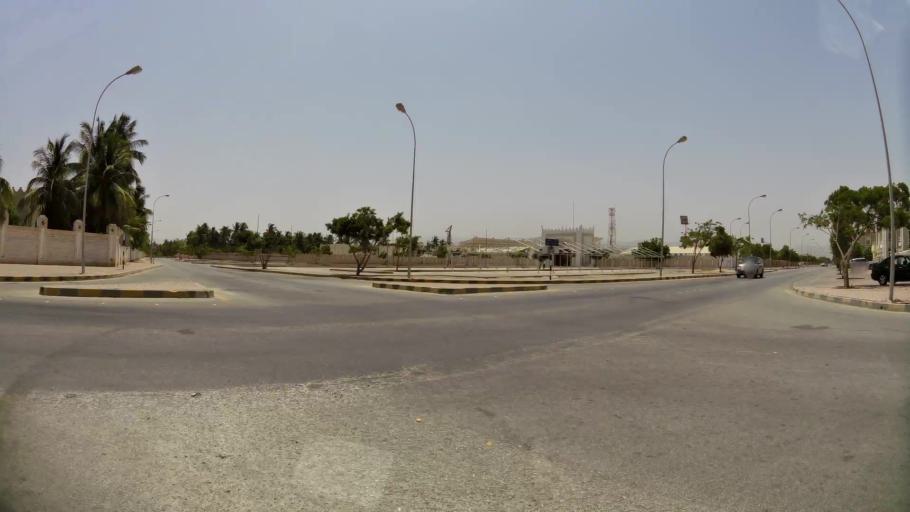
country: OM
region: Zufar
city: Salalah
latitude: 17.0164
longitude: 54.0758
